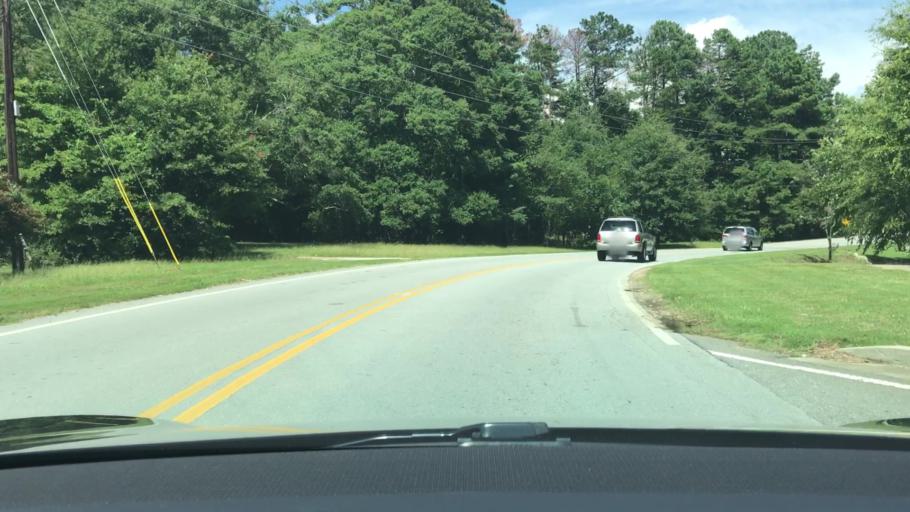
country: US
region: Georgia
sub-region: Gwinnett County
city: Sugar Hill
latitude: 34.0808
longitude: -84.0549
